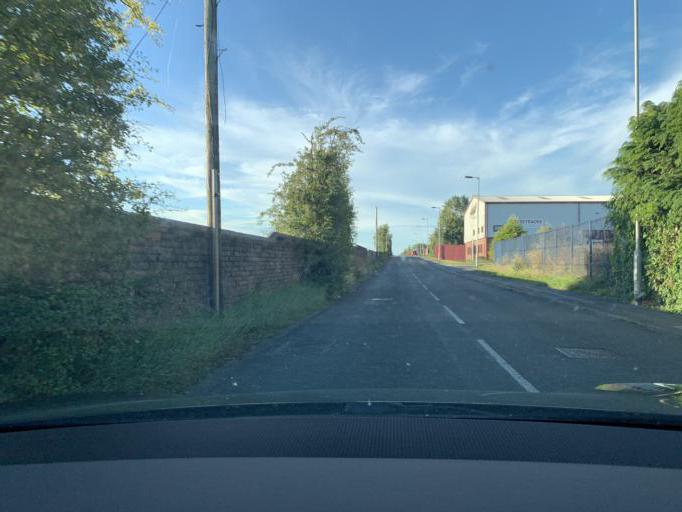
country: GB
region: England
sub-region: Staffordshire
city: Stafford
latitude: 52.8238
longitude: -2.1176
